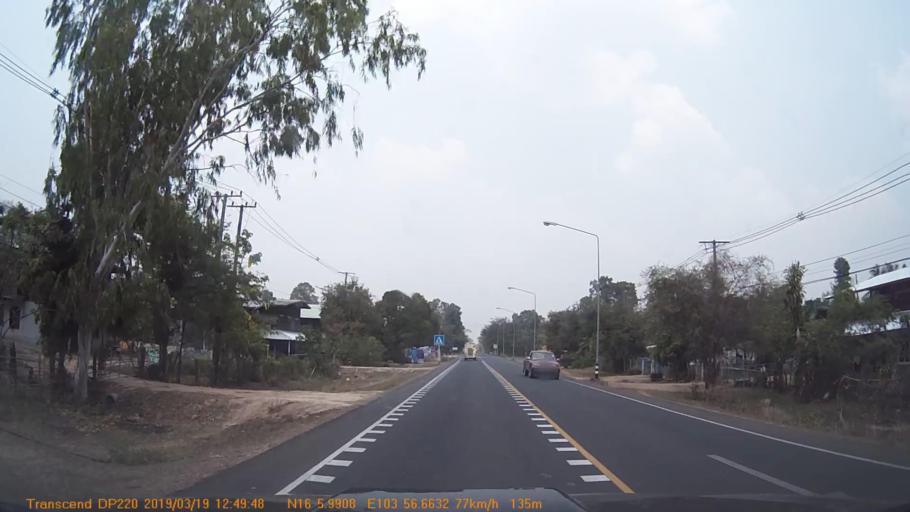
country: TH
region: Roi Et
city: Selaphum
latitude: 16.1002
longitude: 103.9444
